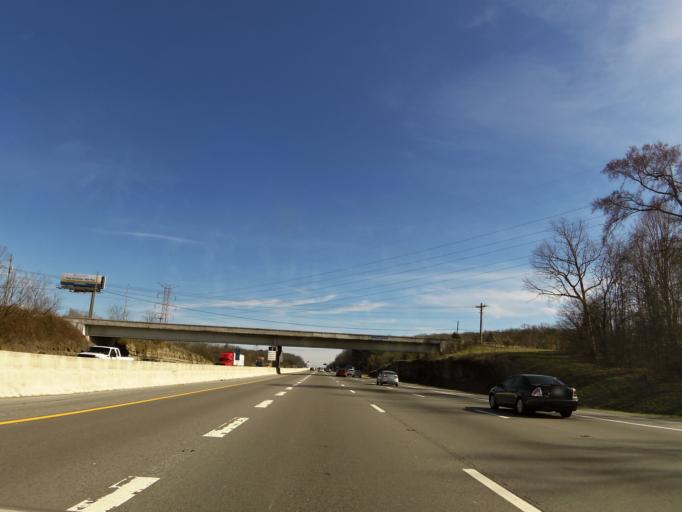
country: US
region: Tennessee
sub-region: Rutherford County
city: La Vergne
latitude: 36.0322
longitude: -86.6405
